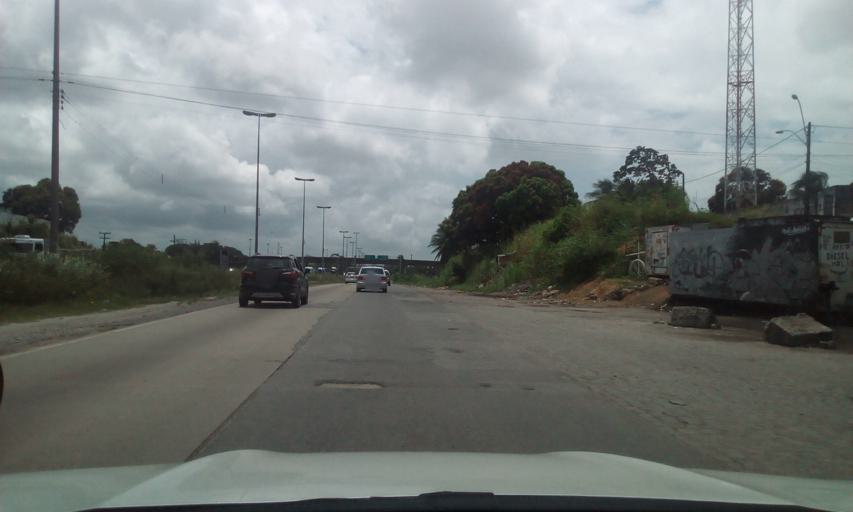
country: BR
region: Pernambuco
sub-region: Recife
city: Recife
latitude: -8.0782
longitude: -34.9429
